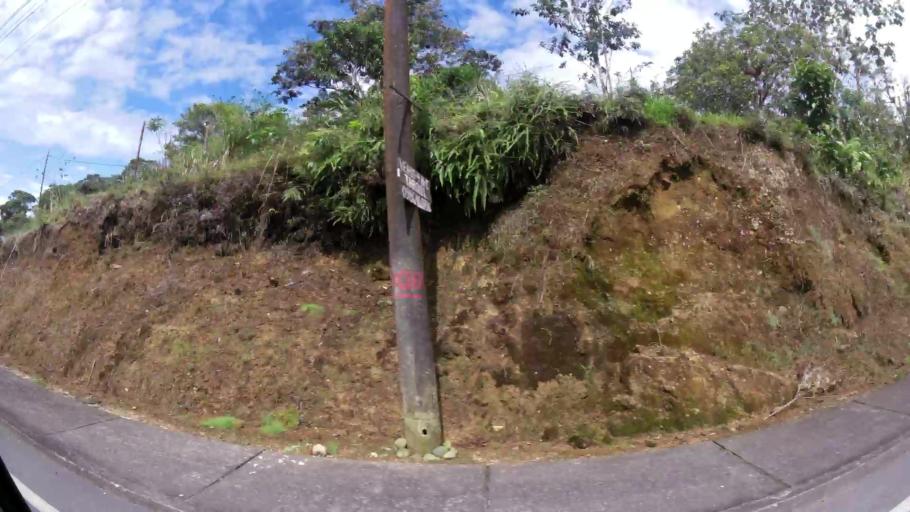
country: EC
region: Pastaza
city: Puyo
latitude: -1.5011
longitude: -78.0247
